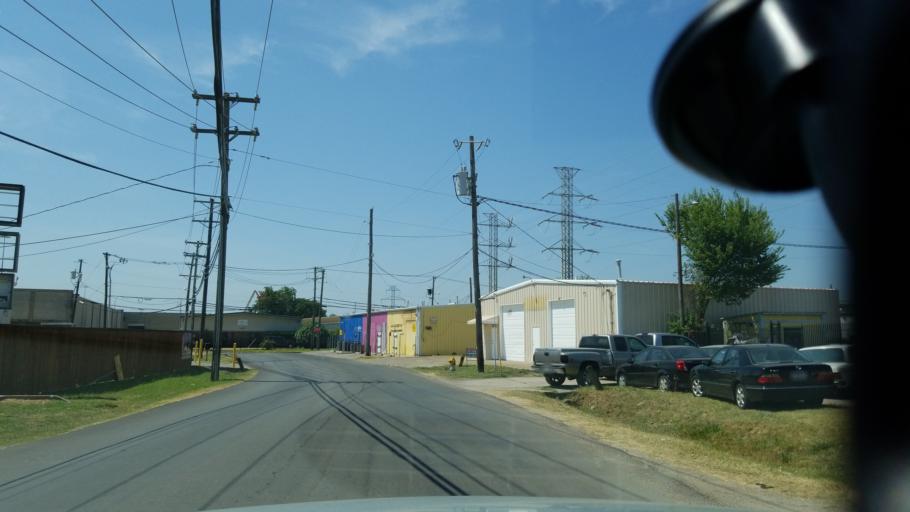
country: US
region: Texas
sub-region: Dallas County
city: Farmers Branch
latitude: 32.8939
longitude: -96.8994
